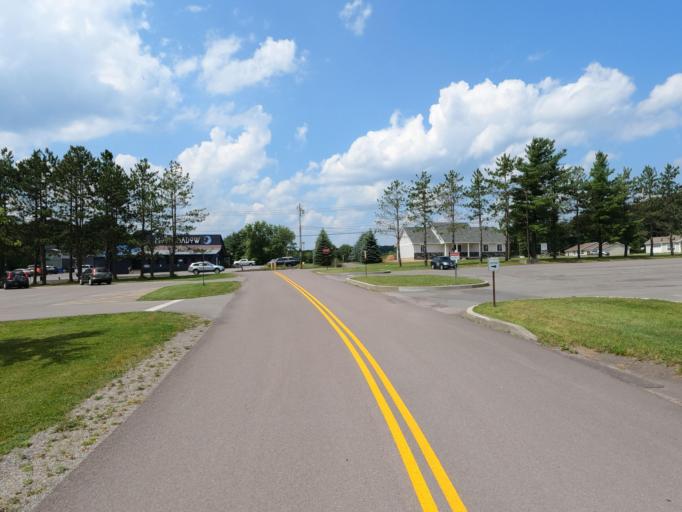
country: US
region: Maryland
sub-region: Garrett County
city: Oakland
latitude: 39.5599
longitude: -79.3453
